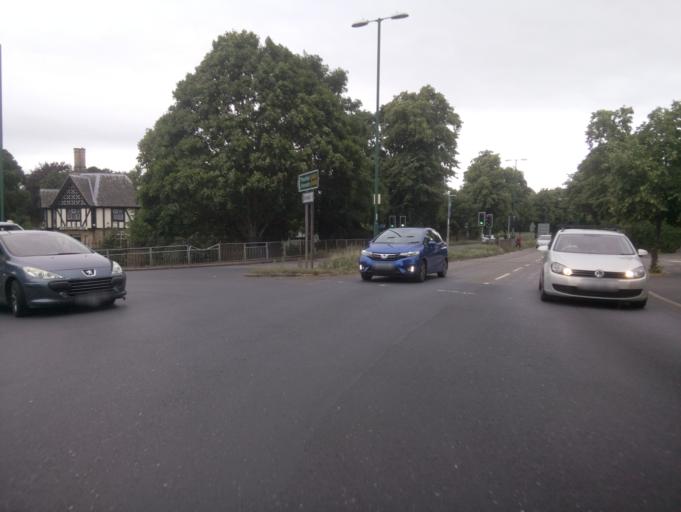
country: GB
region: England
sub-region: Nottinghamshire
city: Arnold
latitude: 52.9886
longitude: -1.1491
